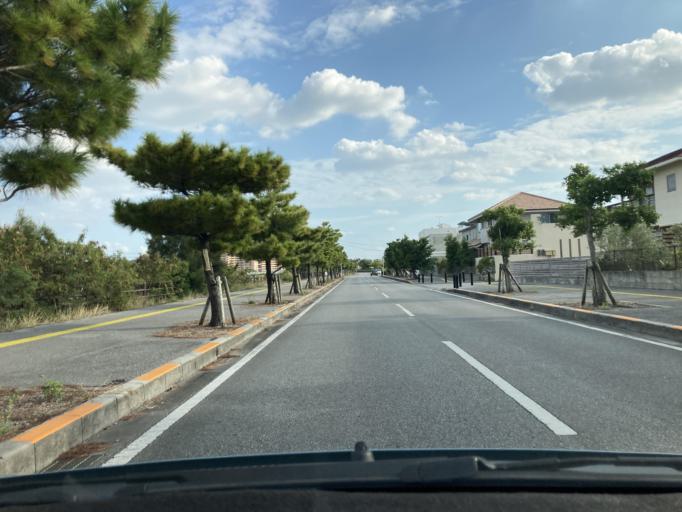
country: JP
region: Okinawa
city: Itoman
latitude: 26.1558
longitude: 127.6662
